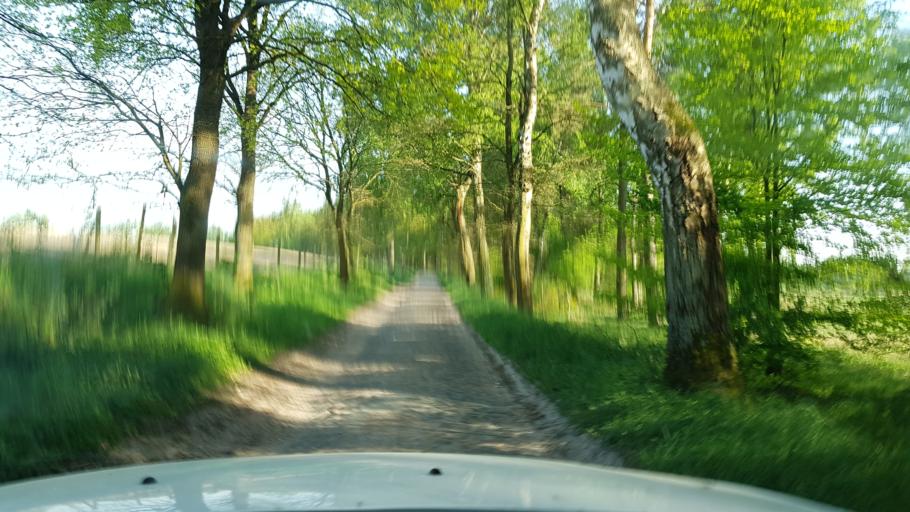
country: PL
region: West Pomeranian Voivodeship
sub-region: Powiat lobeski
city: Resko
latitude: 53.7180
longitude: 15.3312
